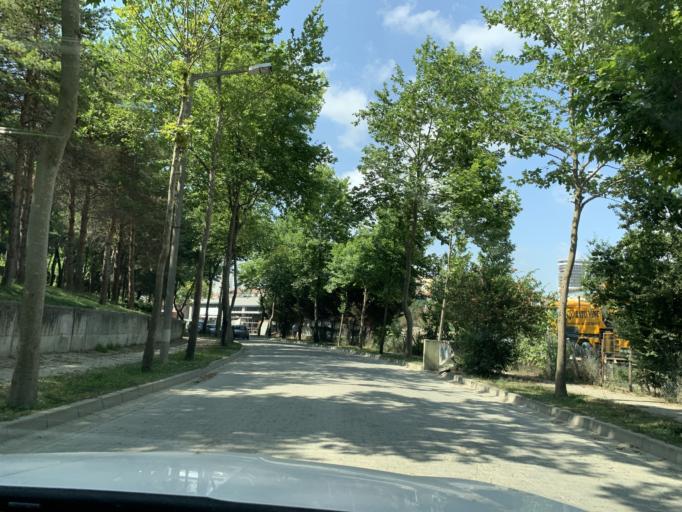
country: TR
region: Istanbul
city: Esenyurt
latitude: 41.0622
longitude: 28.6975
